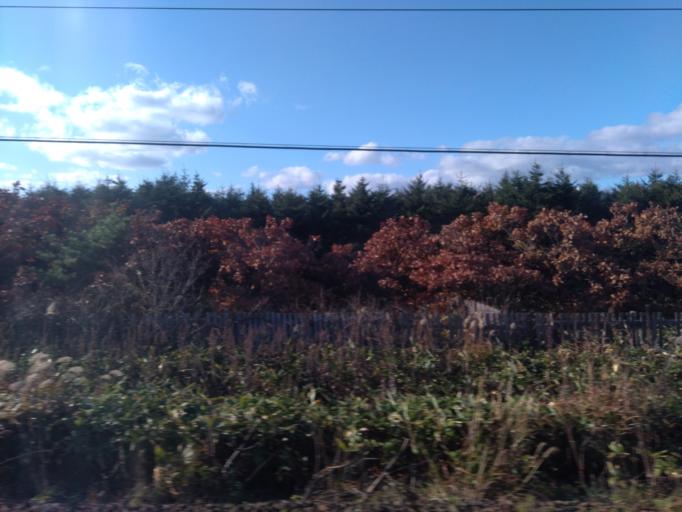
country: JP
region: Hokkaido
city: Niseko Town
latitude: 42.5459
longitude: 140.4122
